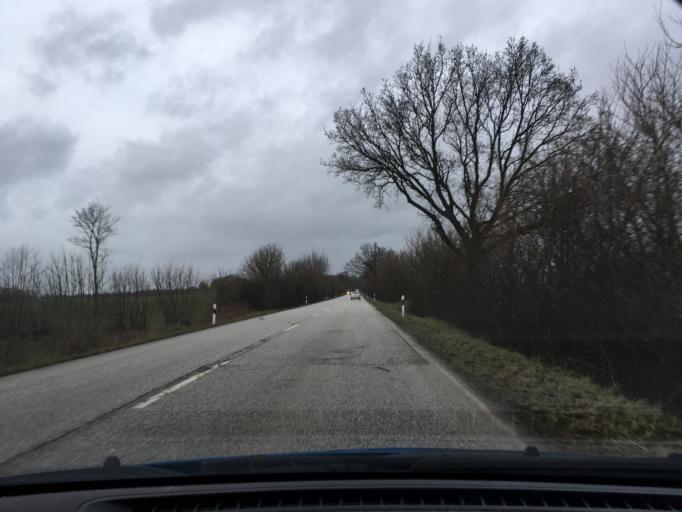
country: DE
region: Schleswig-Holstein
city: Kruzen
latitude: 53.4085
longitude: 10.5376
